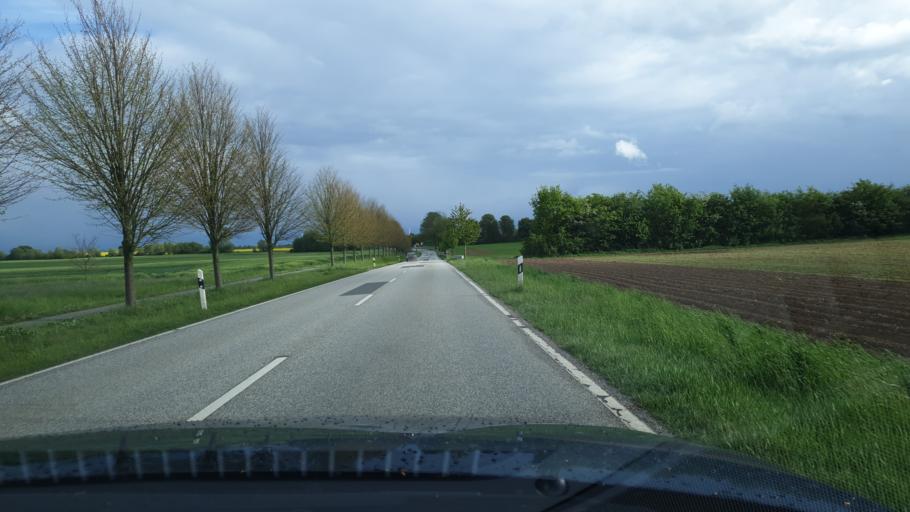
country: DE
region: Mecklenburg-Vorpommern
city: Muhlen Eichsen
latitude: 53.7210
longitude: 11.2862
